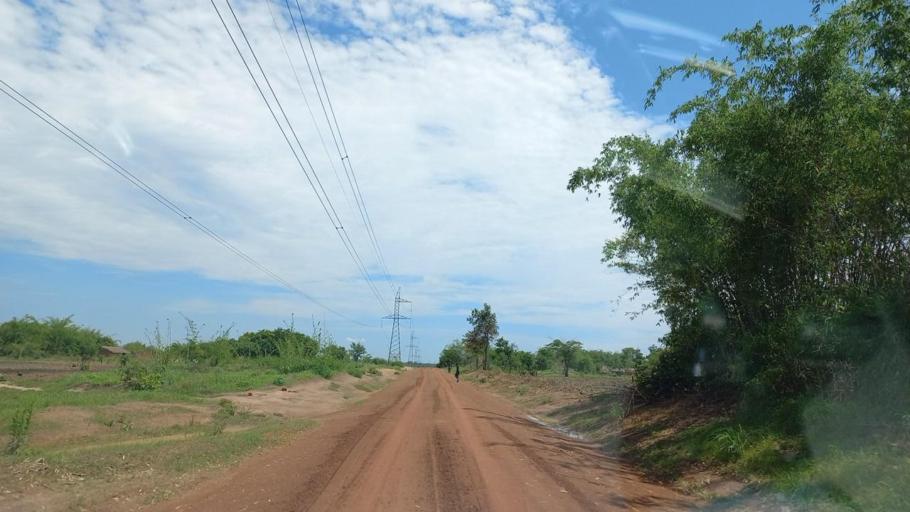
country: ZM
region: Copperbelt
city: Kitwe
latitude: -12.8402
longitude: 28.3400
